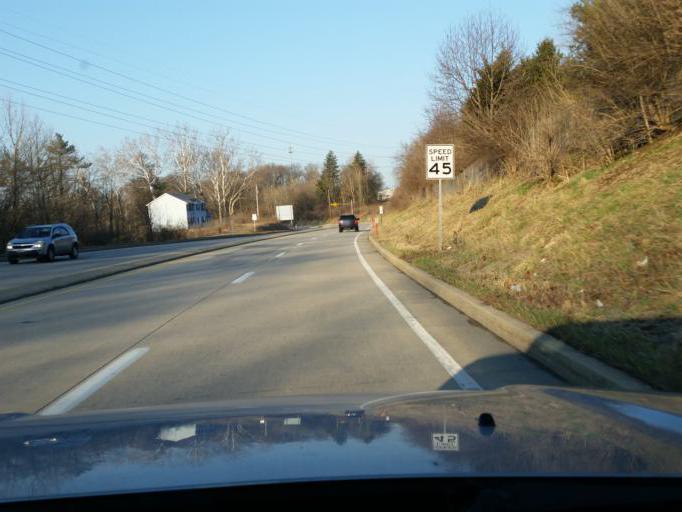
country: US
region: Pennsylvania
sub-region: Lancaster County
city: Lancaster
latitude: 40.0530
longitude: -76.2744
